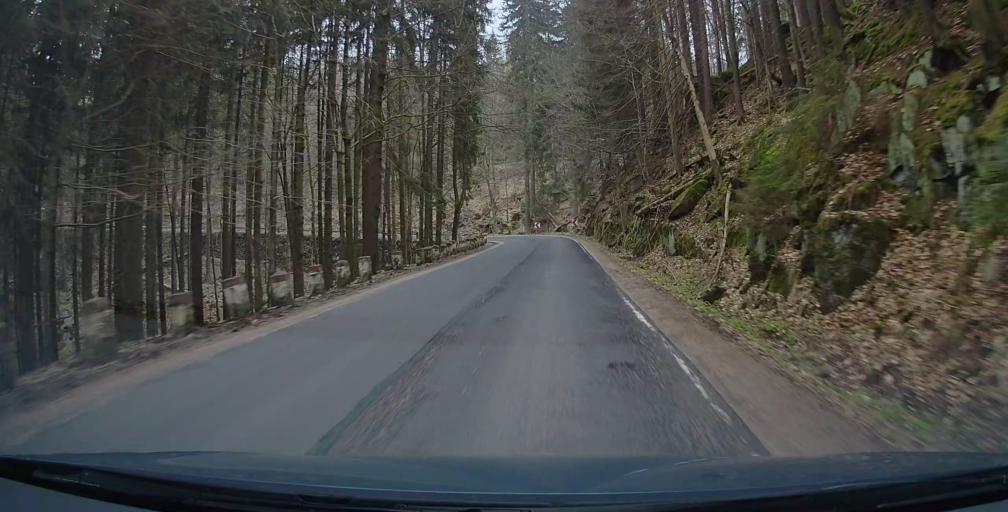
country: PL
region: Lower Silesian Voivodeship
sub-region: Powiat klodzki
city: Radkow
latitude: 50.4777
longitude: 16.3924
